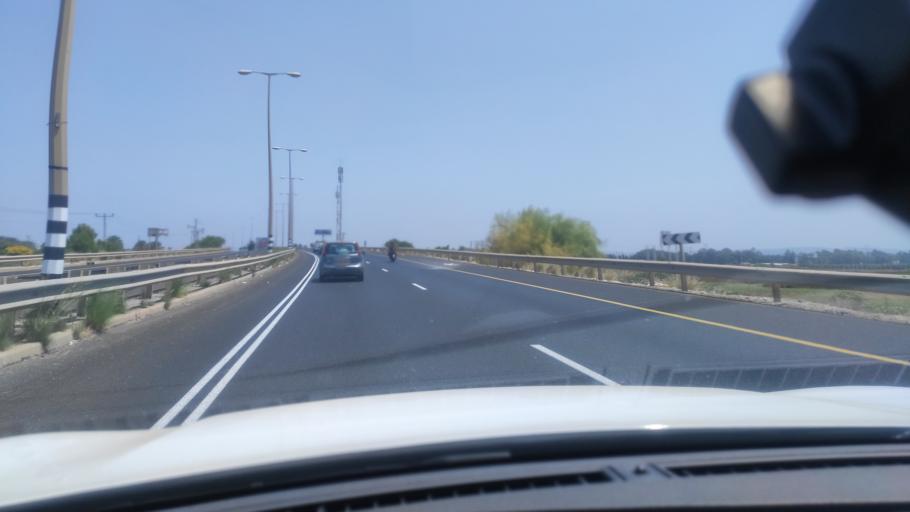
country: IL
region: Central District
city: Petah Tiqwa
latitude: 32.1091
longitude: 34.9018
